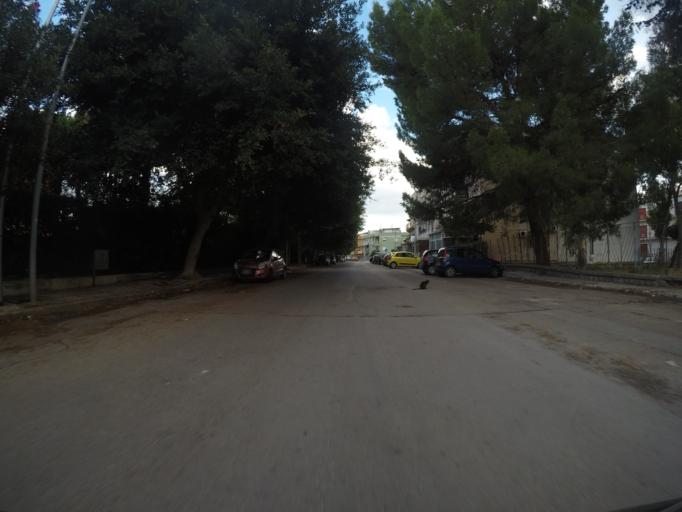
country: IT
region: Sicily
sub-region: Palermo
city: Isola delle Femmine
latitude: 38.1990
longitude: 13.3097
